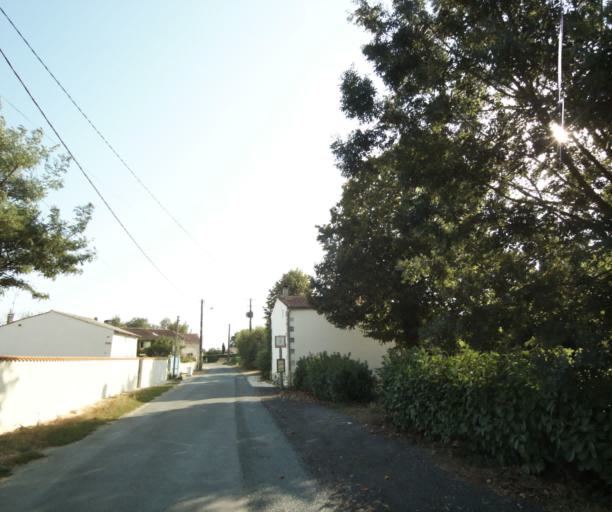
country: FR
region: Poitou-Charentes
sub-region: Departement de la Charente-Maritime
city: Cabariot
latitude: 45.9619
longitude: -0.8395
